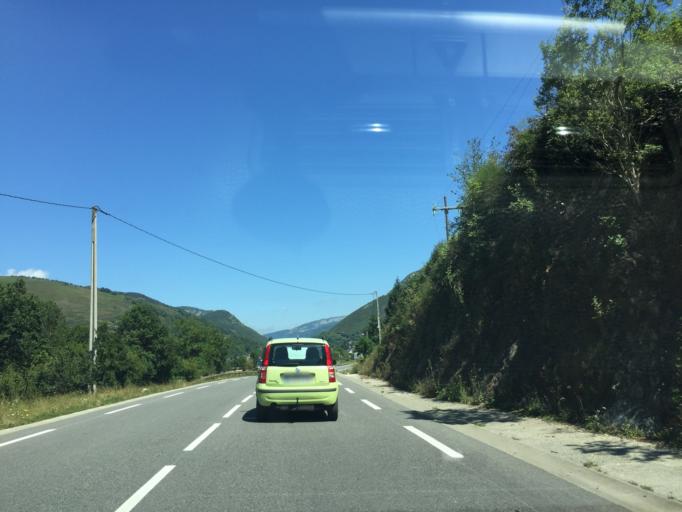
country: FR
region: Midi-Pyrenees
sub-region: Departement des Hautes-Pyrenees
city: Saint-Lary-Soulan
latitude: 42.8923
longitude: 0.3530
